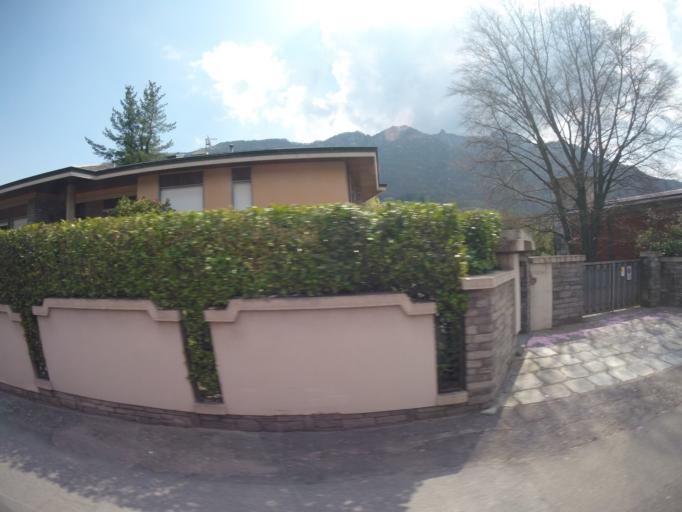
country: IT
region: Piedmont
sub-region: Provincia Verbano-Cusio-Ossola
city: Gabbio-Cereda-Ramate
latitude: 45.9042
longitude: 8.4193
